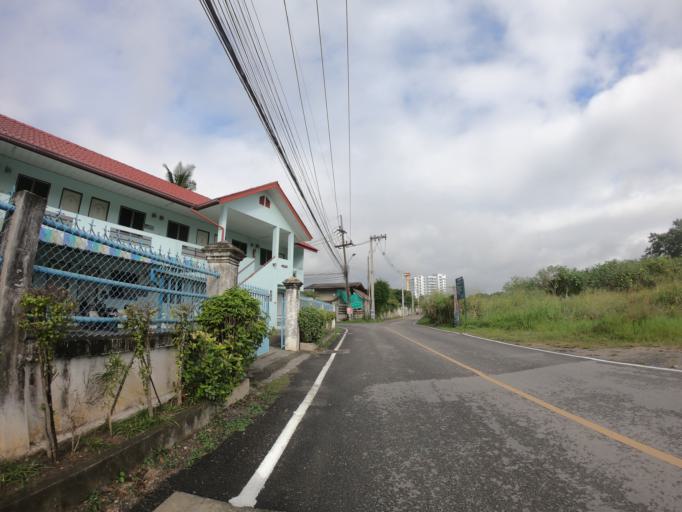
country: TH
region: Chiang Mai
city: Chiang Mai
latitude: 18.8158
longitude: 98.9651
